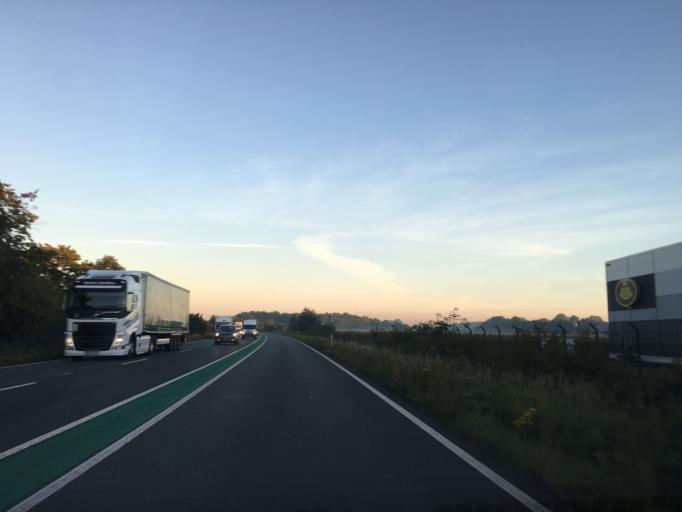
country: DE
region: North Rhine-Westphalia
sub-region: Regierungsbezirk Munster
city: Laer
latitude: 52.0924
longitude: 7.4126
